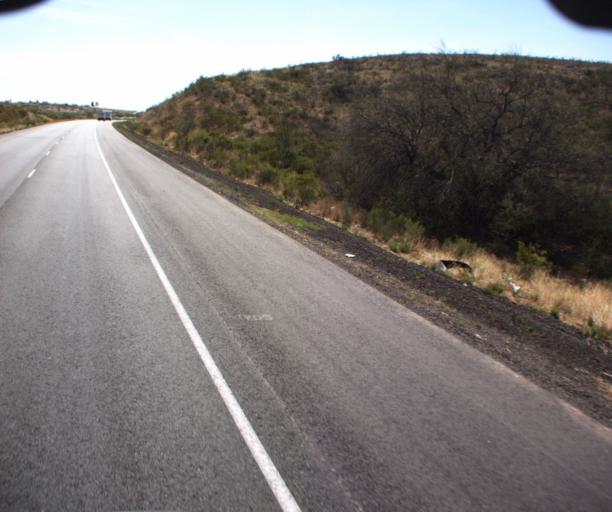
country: US
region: Arizona
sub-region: Cochise County
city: Mescal
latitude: 31.9685
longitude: -110.4721
